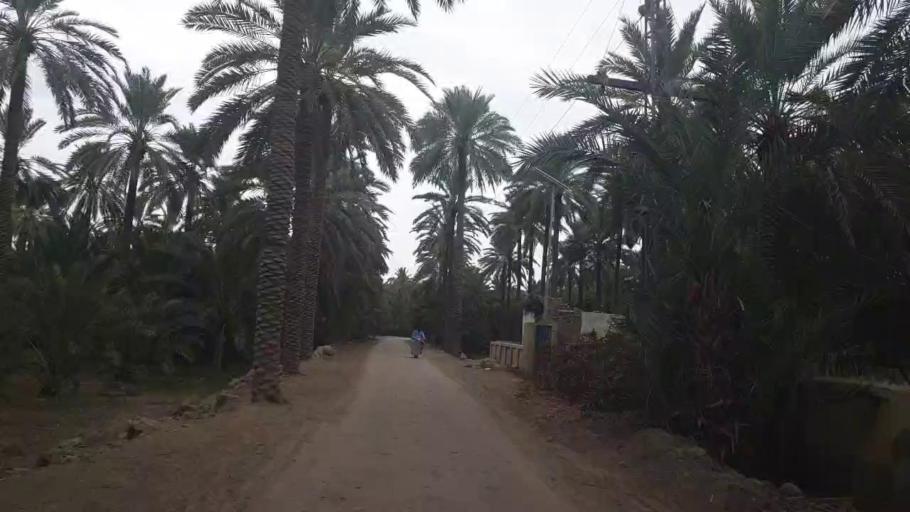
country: PK
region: Sindh
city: Khairpur
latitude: 27.5734
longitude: 68.7447
